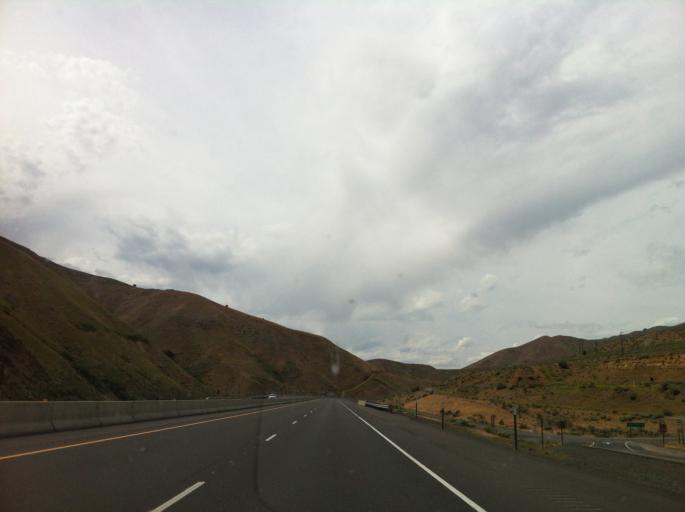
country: US
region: Idaho
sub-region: Washington County
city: Weiser
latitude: 44.4268
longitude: -117.3141
